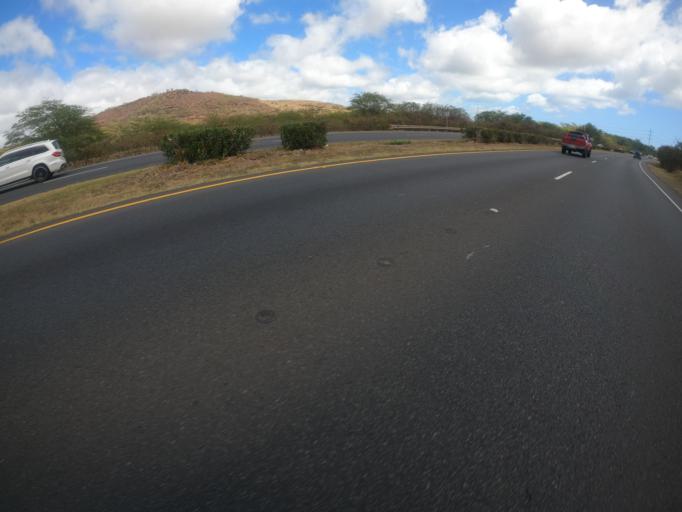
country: US
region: Hawaii
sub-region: Honolulu County
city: Makakilo City
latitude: 21.3362
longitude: -158.0961
